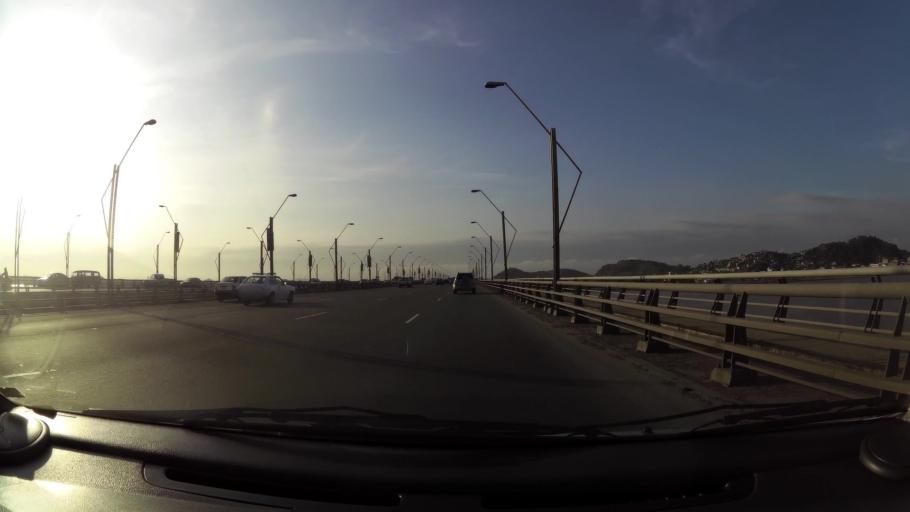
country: EC
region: Guayas
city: Eloy Alfaro
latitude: -2.1611
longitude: -79.8515
